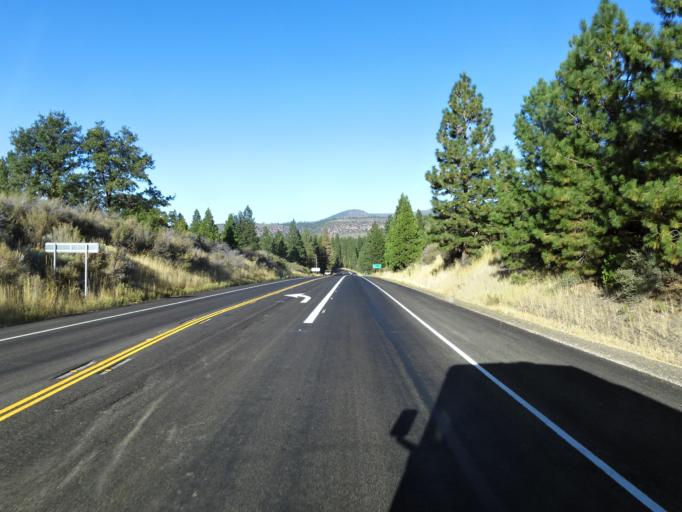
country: US
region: California
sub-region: Siskiyou County
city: Weed
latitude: 41.4445
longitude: -122.3713
